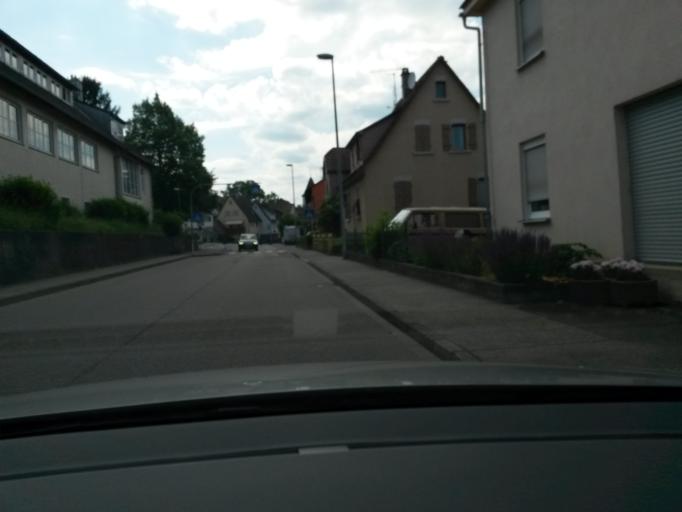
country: DE
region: Baden-Wuerttemberg
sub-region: Regierungsbezirk Stuttgart
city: Vaihingen an der Enz
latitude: 48.9520
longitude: 8.9711
